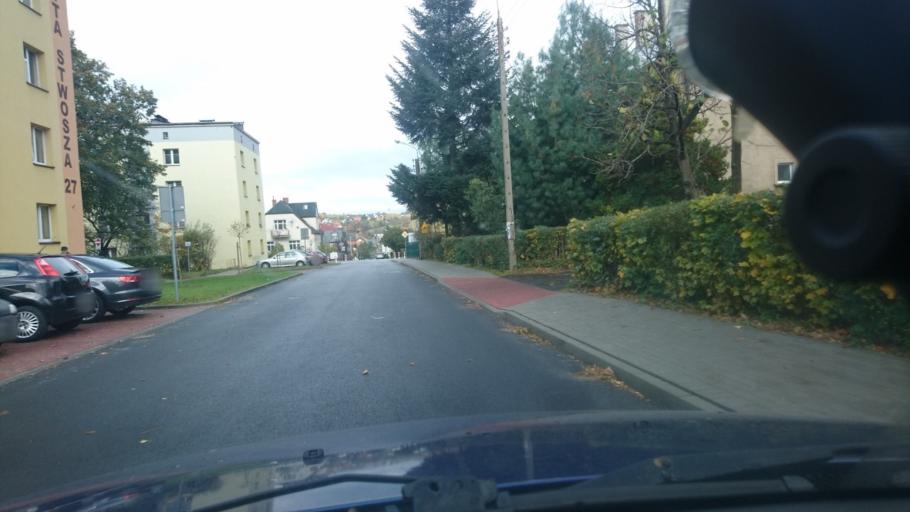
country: PL
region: Silesian Voivodeship
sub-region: Bielsko-Biala
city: Bielsko-Biala
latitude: 49.8254
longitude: 19.0285
